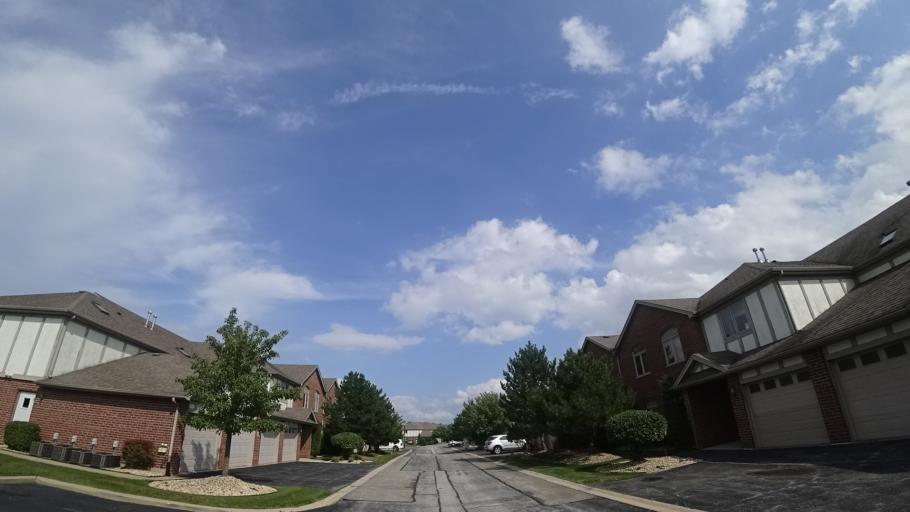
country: US
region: Illinois
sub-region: Cook County
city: Tinley Park
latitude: 41.5585
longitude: -87.7697
